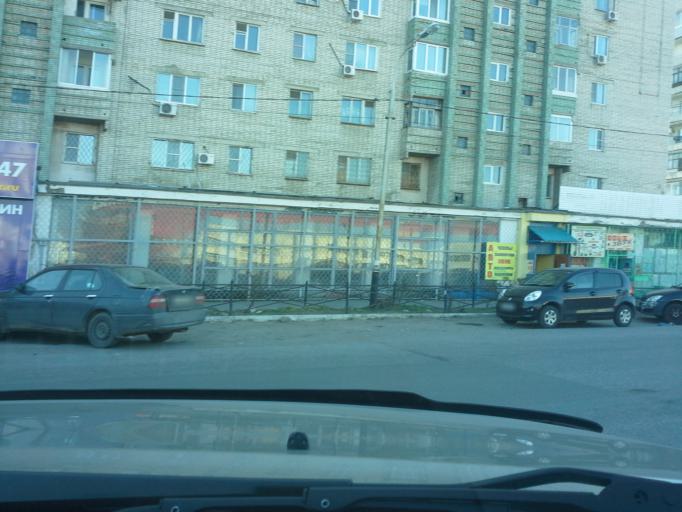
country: RU
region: Khabarovsk Krai
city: Khabarovsk Vtoroy
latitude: 48.4256
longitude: 135.1076
